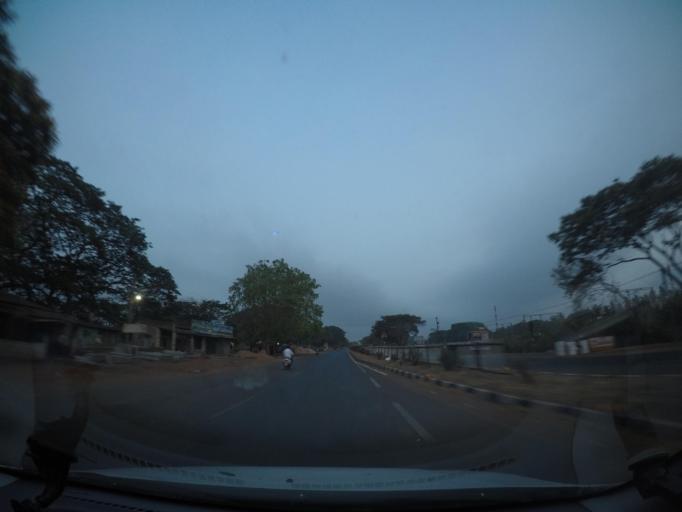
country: IN
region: Andhra Pradesh
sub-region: West Godavari
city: Tadepallegudem
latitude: 16.8195
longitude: 81.3996
